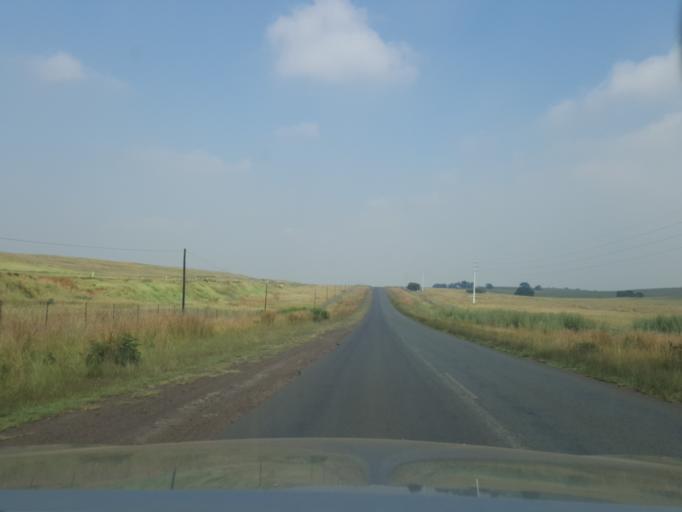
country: ZA
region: Mpumalanga
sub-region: Nkangala District Municipality
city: Witbank
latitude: -26.0145
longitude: 29.3348
